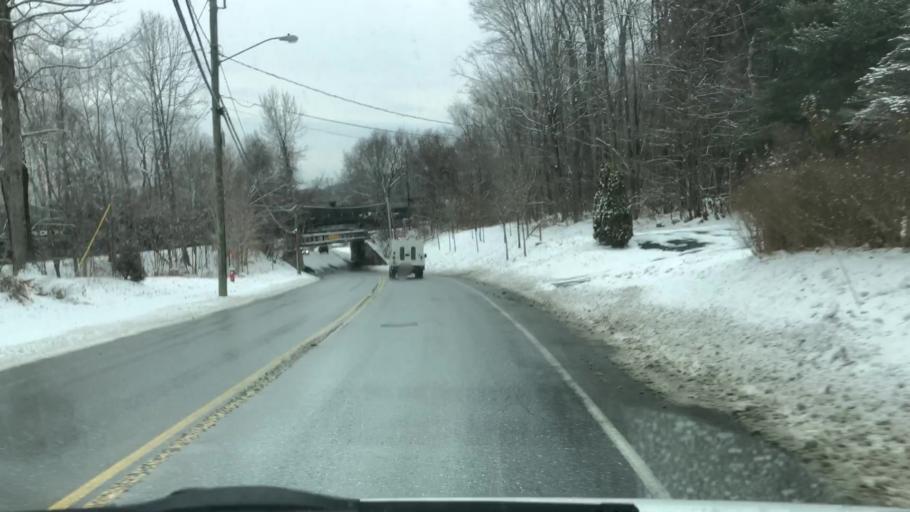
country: US
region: Massachusetts
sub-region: Berkshire County
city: Dalton
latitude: 42.4637
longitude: -73.1811
